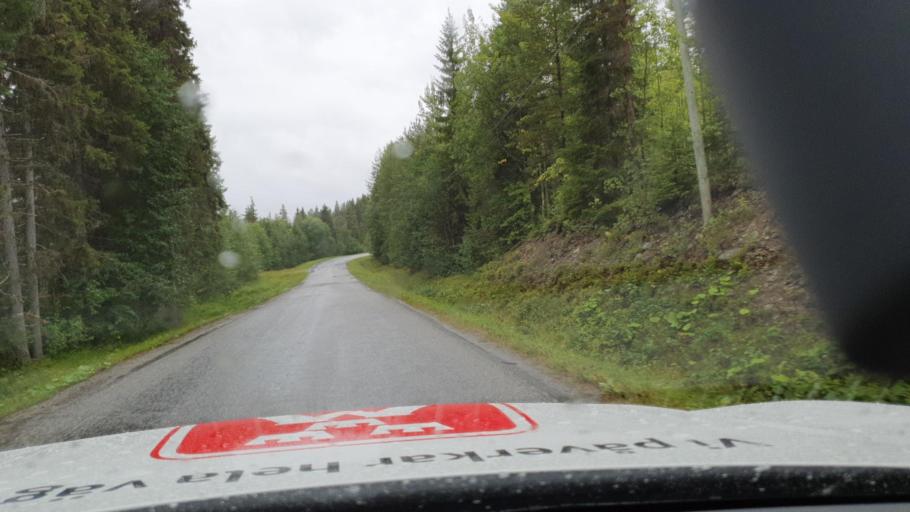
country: SE
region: Vaesterbotten
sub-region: Dorotea Kommun
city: Dorotea
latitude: 64.1274
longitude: 16.2308
